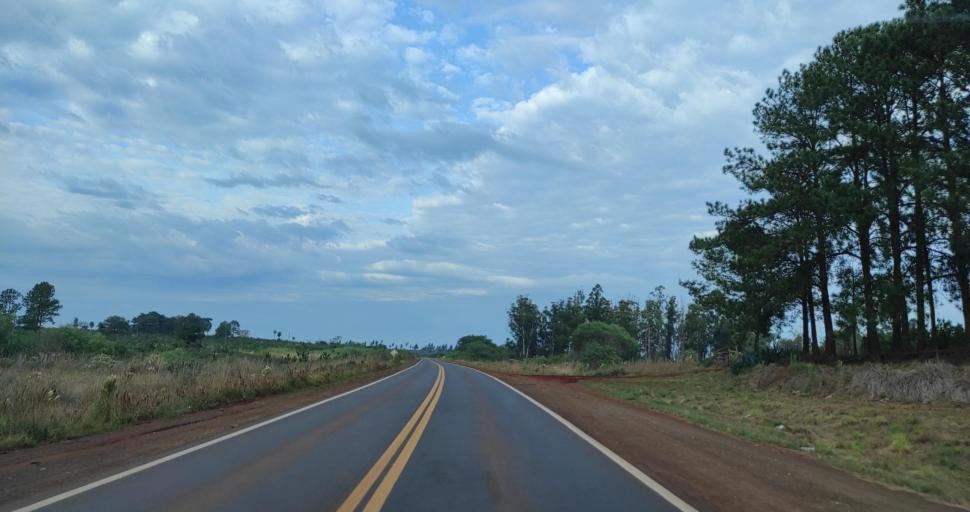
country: AR
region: Corrientes
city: San Carlos
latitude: -27.8725
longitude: -55.9309
